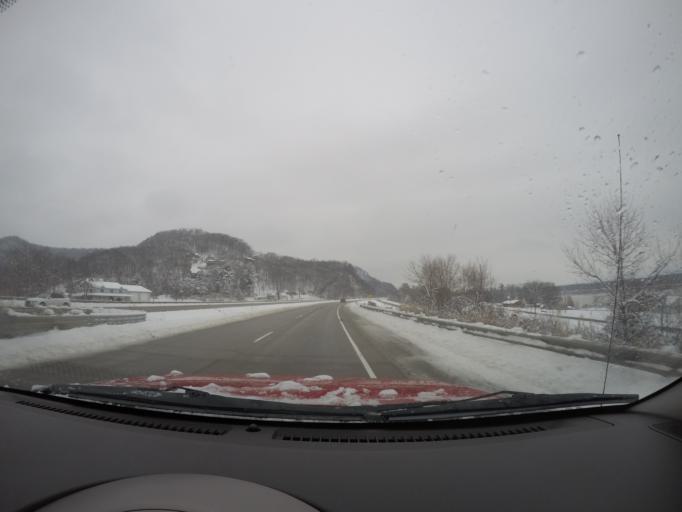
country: US
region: Wisconsin
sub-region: La Crosse County
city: Brice Prairie
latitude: 43.8912
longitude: -91.3425
